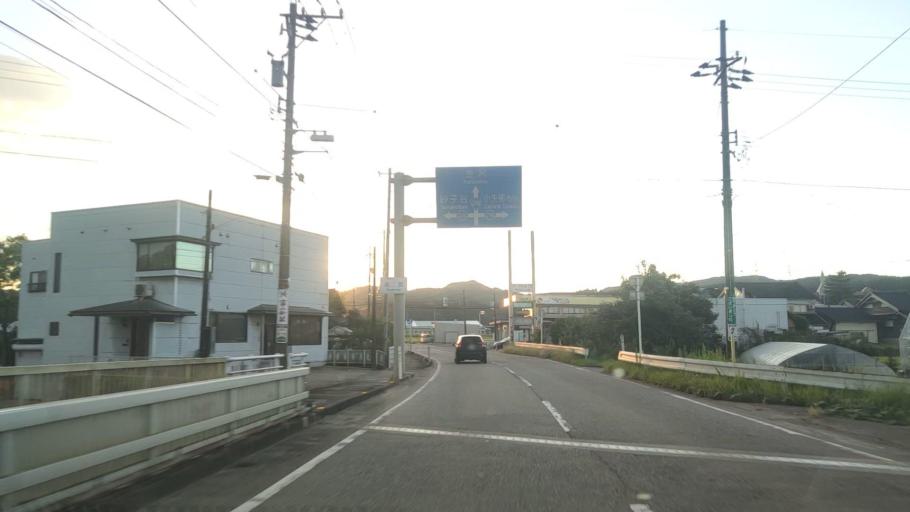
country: JP
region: Toyama
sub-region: Oyabe Shi
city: Oyabe
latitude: 36.6325
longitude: 136.8357
